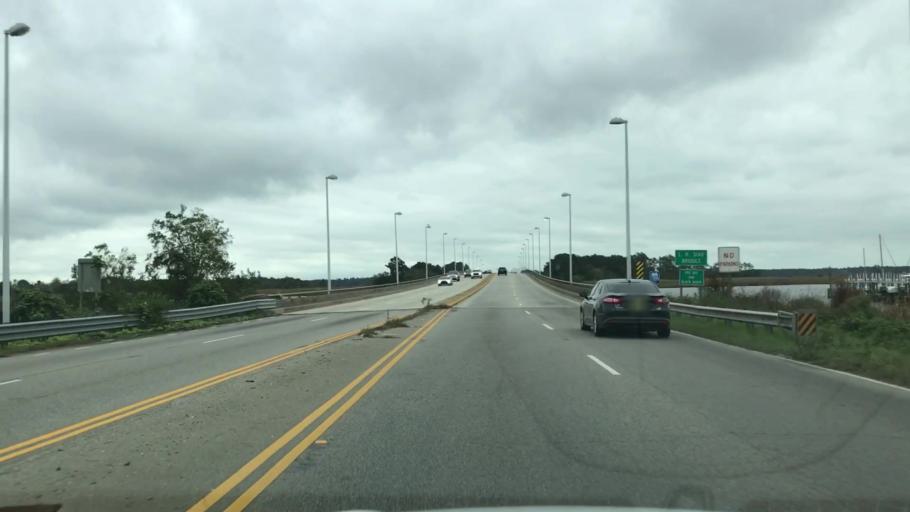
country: US
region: South Carolina
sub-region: Georgetown County
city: Georgetown
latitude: 33.3669
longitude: -79.2685
